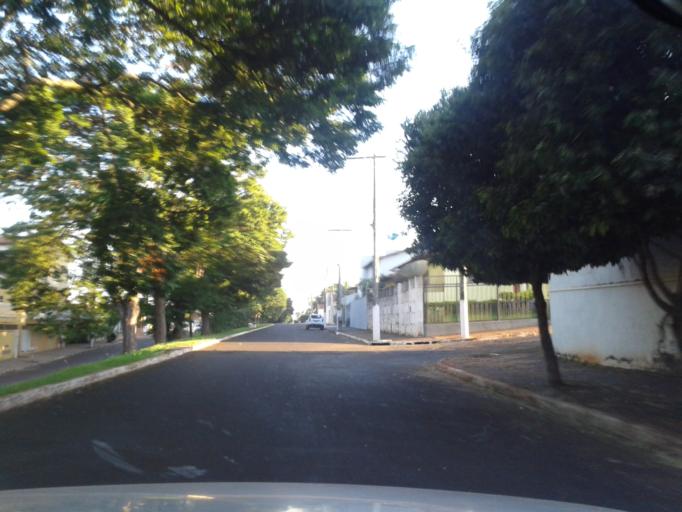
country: BR
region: Minas Gerais
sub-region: Ituiutaba
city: Ituiutaba
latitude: -18.9727
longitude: -49.4671
